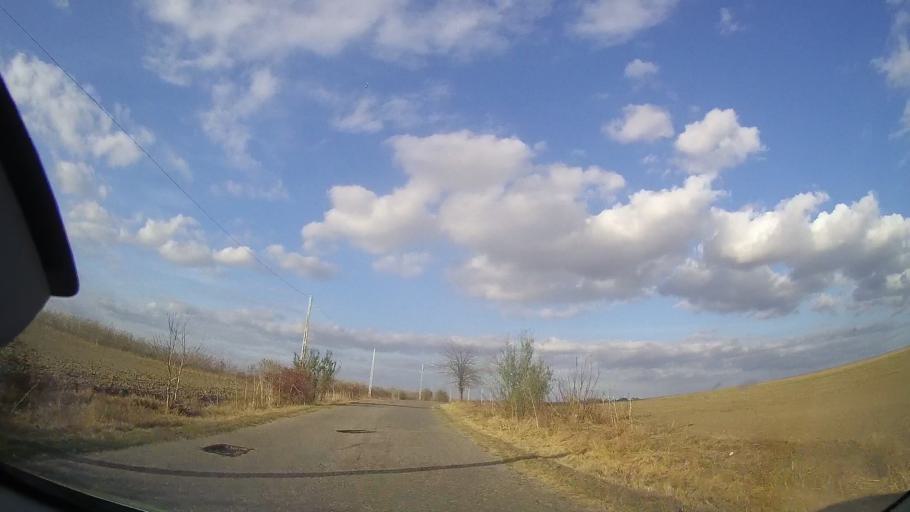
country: RO
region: Constanta
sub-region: Comuna Cerchezu
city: Cerchezu
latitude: 43.8454
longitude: 28.0985
